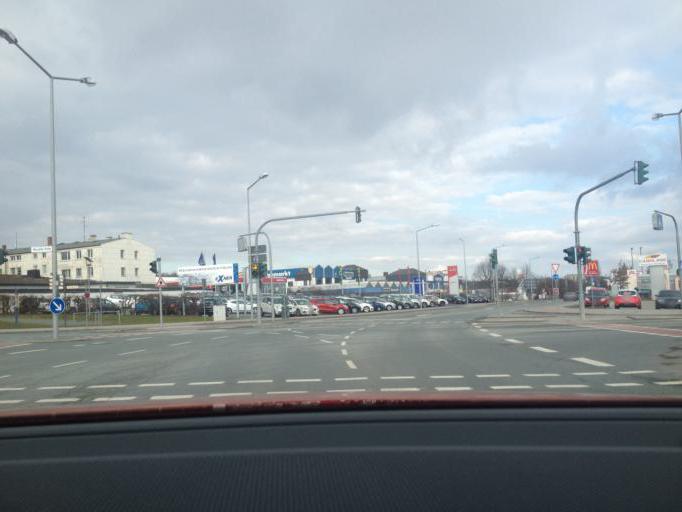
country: DE
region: Bavaria
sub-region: Upper Franconia
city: Hof
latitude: 50.3052
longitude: 11.9183
